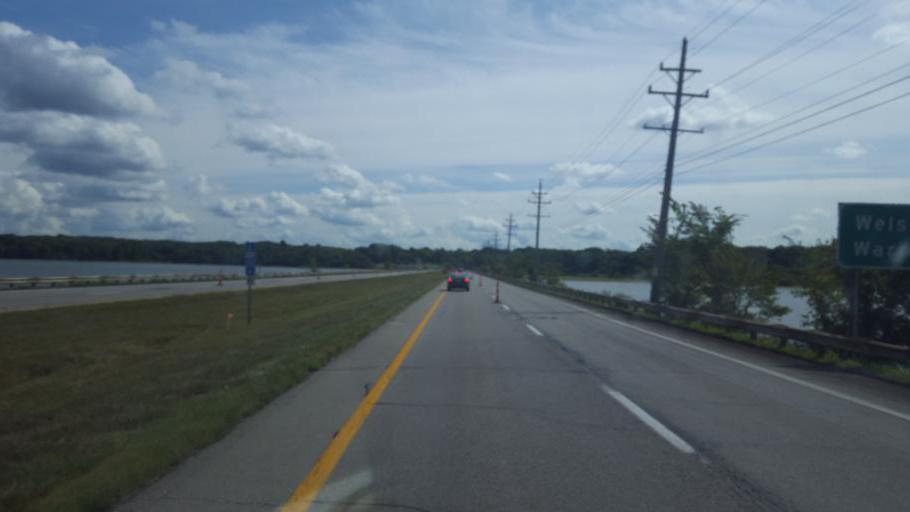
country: US
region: Ohio
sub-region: Portage County
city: Hiram
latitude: 41.3836
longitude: -81.2005
